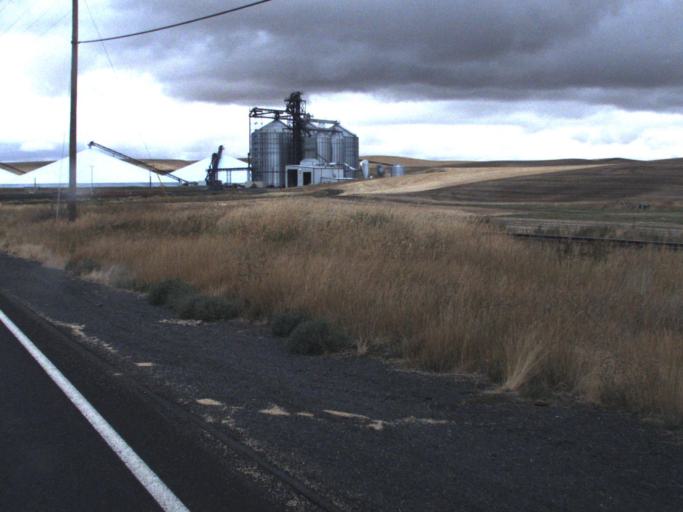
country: US
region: Washington
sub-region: Whitman County
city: Colfax
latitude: 47.1868
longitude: -117.3132
